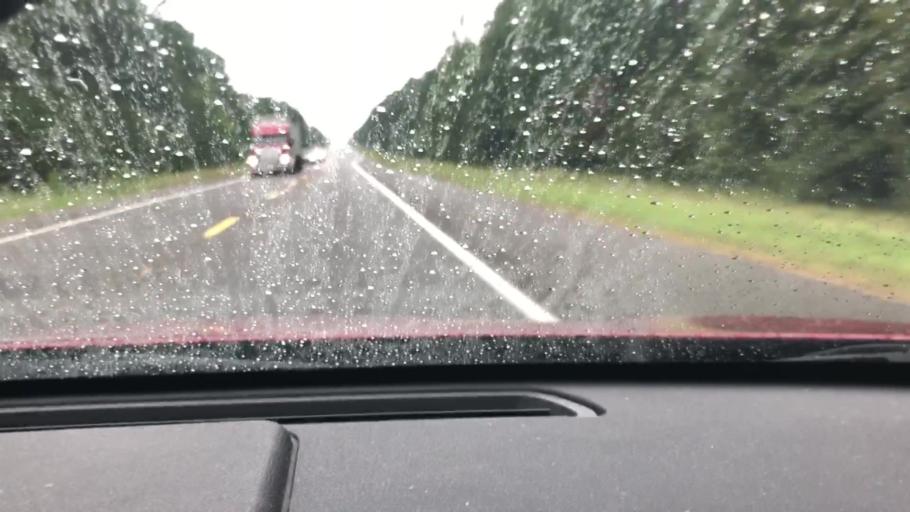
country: US
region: Arkansas
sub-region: Columbia County
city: Magnolia
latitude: 33.3054
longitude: -93.2732
